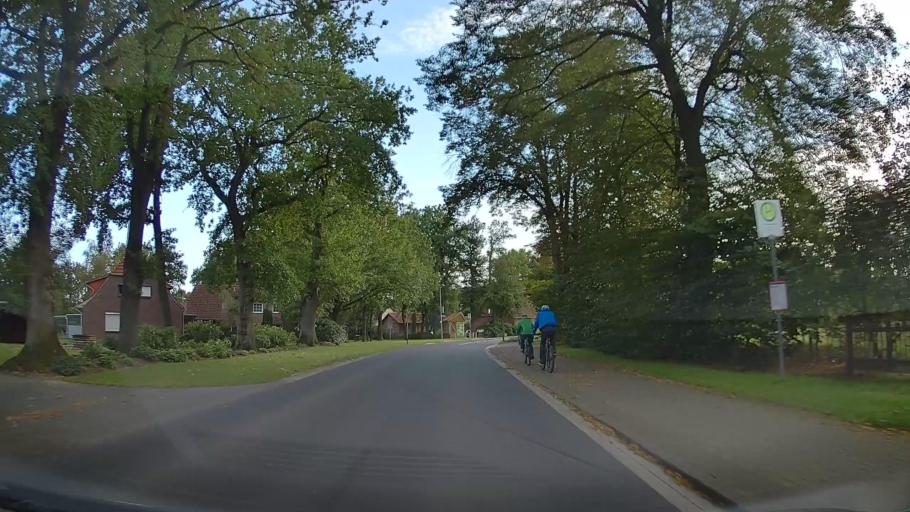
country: DE
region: Lower Saxony
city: Hassendorf
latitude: 53.1064
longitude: 9.2651
